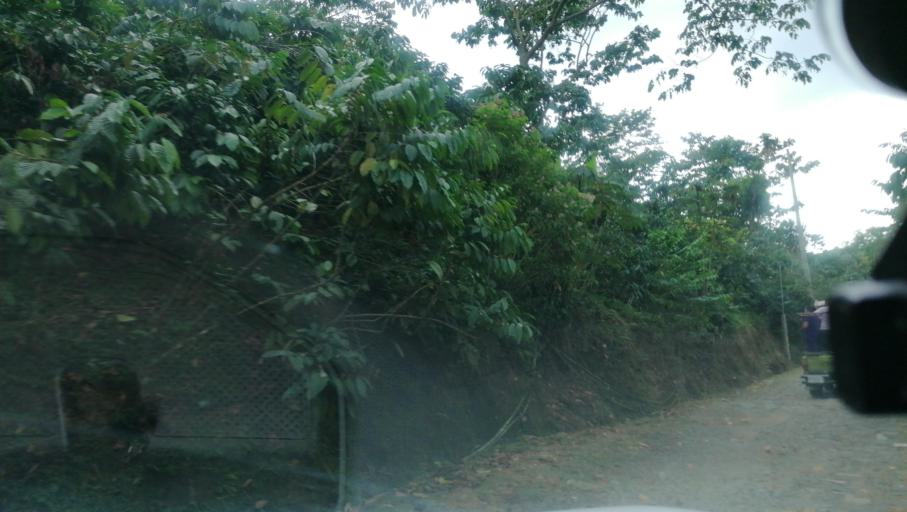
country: MX
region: Chiapas
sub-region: Cacahoatan
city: Benito Juarez
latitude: 15.0711
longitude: -92.1673
